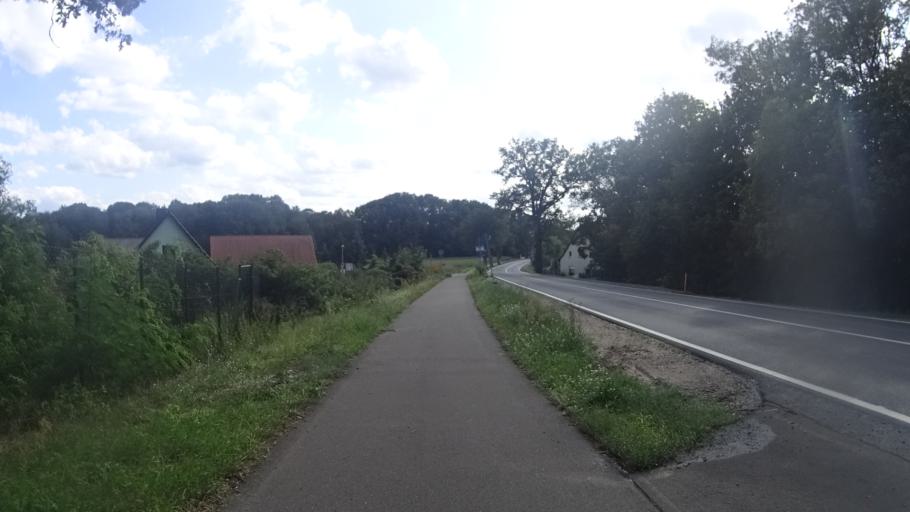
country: DE
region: Brandenburg
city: Rhinow
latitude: 52.6893
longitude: 12.3642
